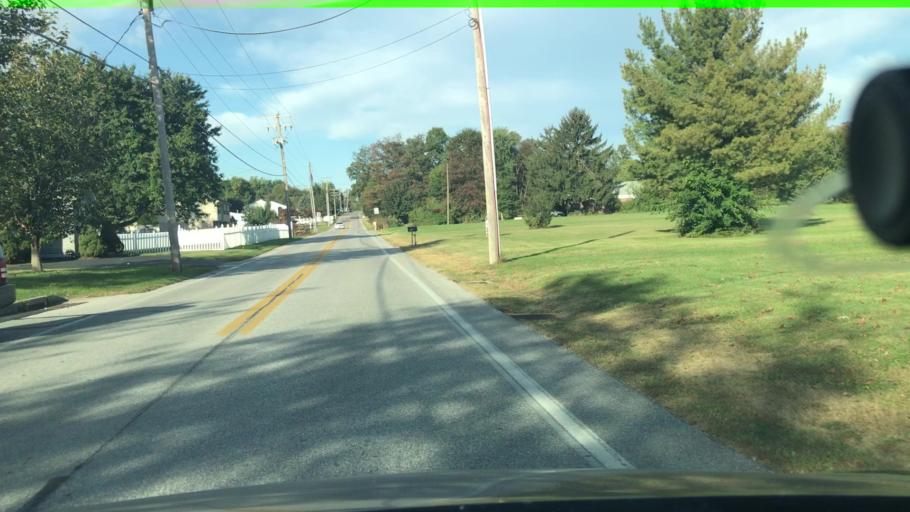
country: US
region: Pennsylvania
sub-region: York County
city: Weigelstown
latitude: 40.0183
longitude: -76.8038
